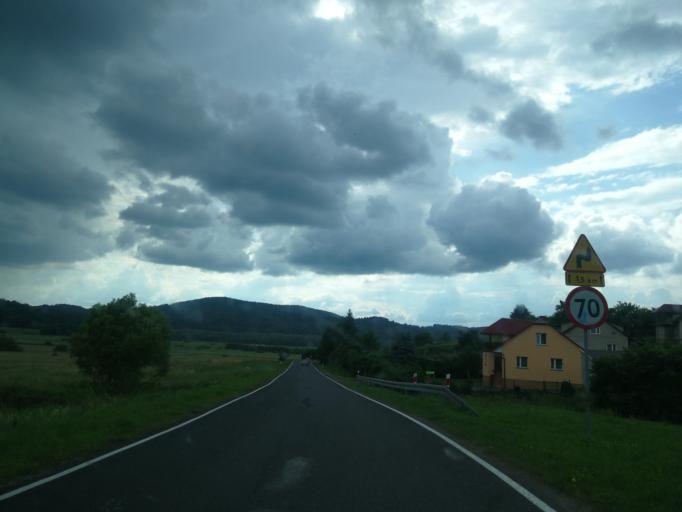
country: PL
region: Subcarpathian Voivodeship
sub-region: Powiat leski
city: Uherce Mineralne
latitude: 49.4579
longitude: 22.4140
